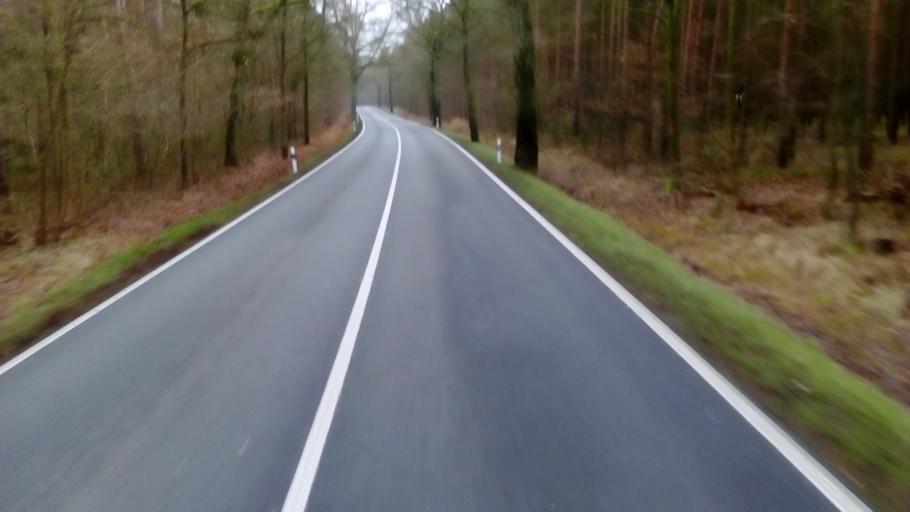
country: DE
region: Brandenburg
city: Heiligengrabe
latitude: 53.1383
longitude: 12.2934
